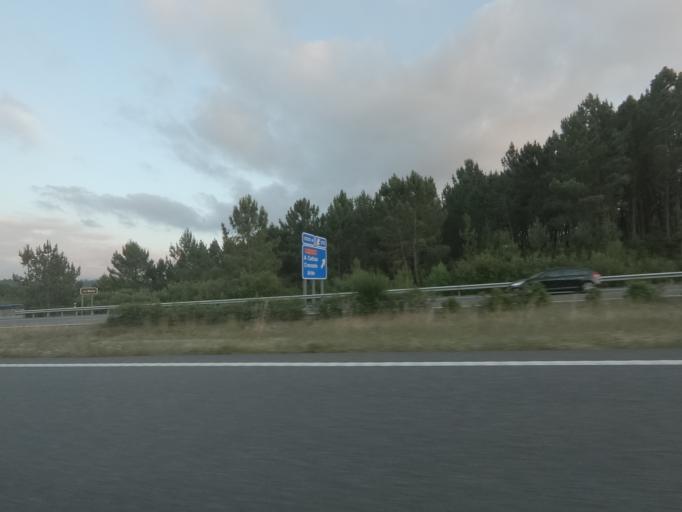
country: ES
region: Galicia
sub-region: Provincia de Pontevedra
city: Covelo
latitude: 42.2013
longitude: -8.2879
